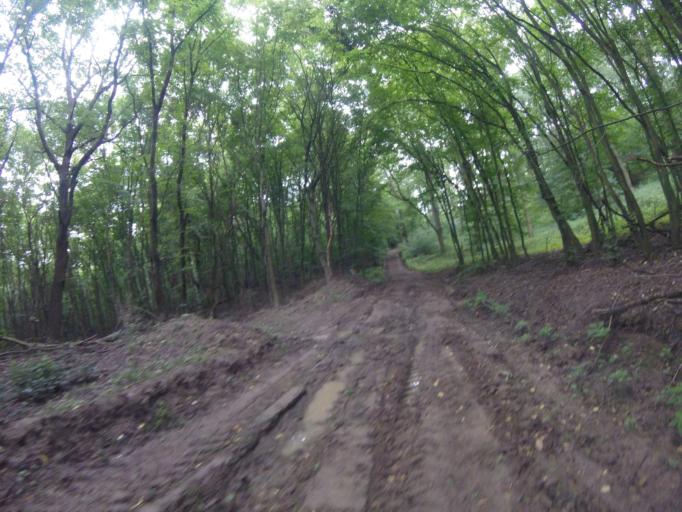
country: SK
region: Nitriansky
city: Sahy
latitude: 48.0536
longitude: 18.9695
